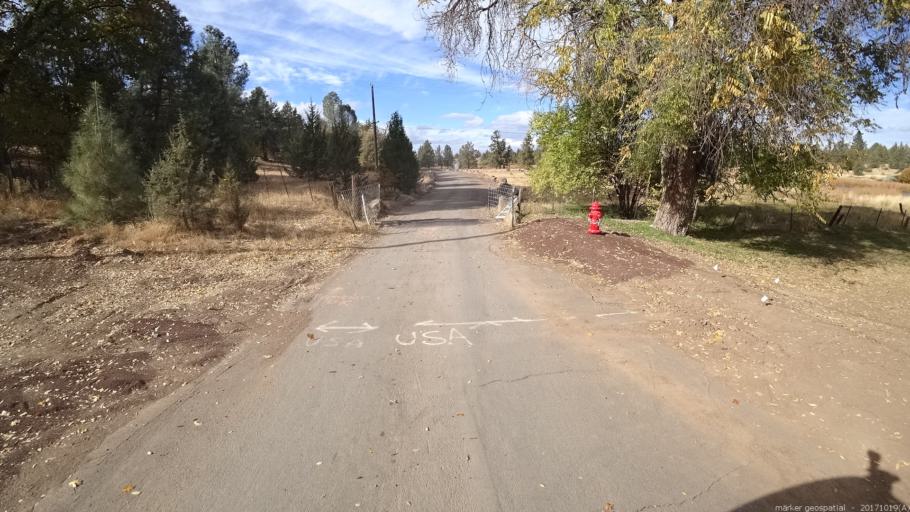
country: US
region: California
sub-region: Shasta County
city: Burney
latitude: 41.0057
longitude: -121.4453
